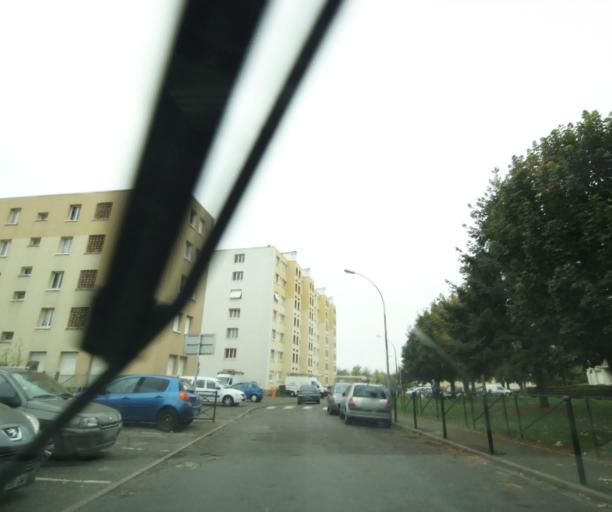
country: FR
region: Centre
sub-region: Departement d'Eure-et-Loir
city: Dreux
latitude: 48.7450
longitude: 1.3606
